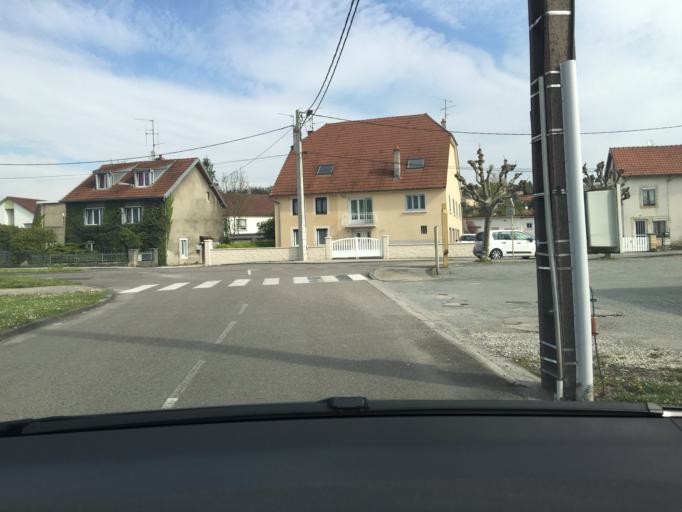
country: FR
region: Franche-Comte
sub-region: Departement du Doubs
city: Bavans
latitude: 47.4792
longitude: 6.7329
